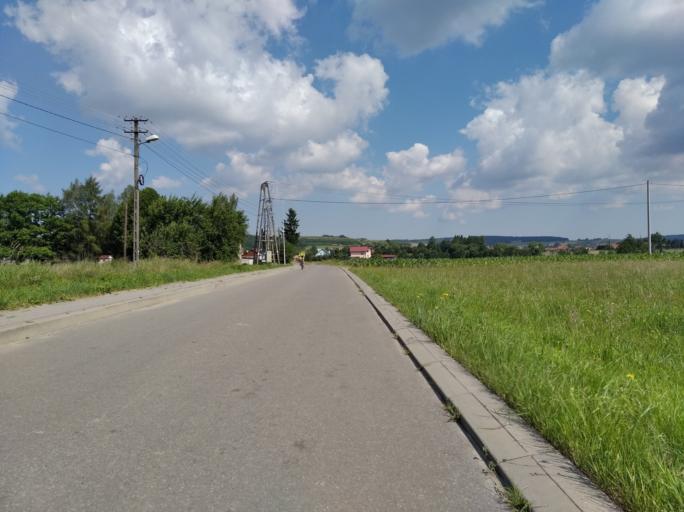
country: PL
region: Subcarpathian Voivodeship
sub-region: Powiat rzeszowski
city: Dynow
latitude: 49.8278
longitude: 22.2271
